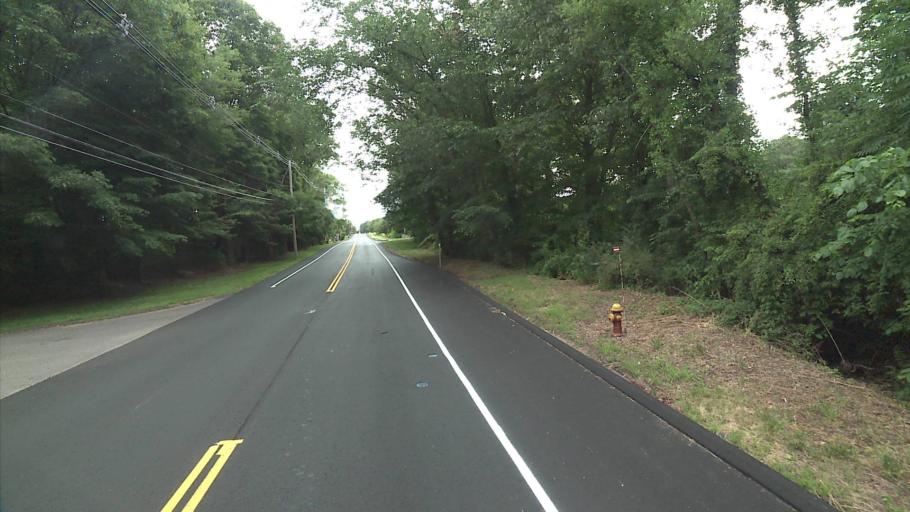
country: US
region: Connecticut
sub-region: New Haven County
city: Wallingford Center
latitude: 41.4217
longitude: -72.8020
